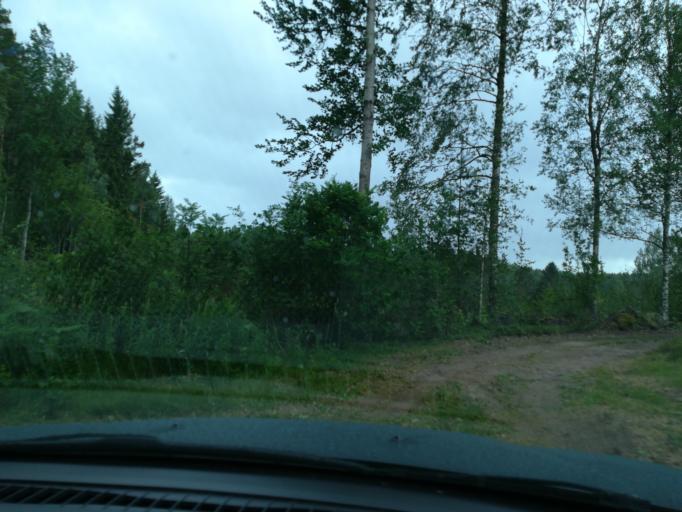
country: FI
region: South Karelia
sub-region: Lappeenranta
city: Savitaipale
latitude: 61.1821
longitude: 27.5542
